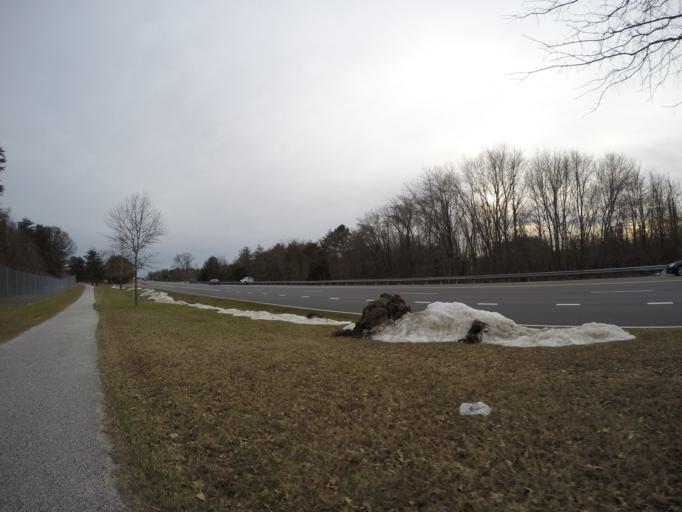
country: US
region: Maryland
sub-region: Anne Arundel County
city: Severn
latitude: 39.1628
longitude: -76.6956
